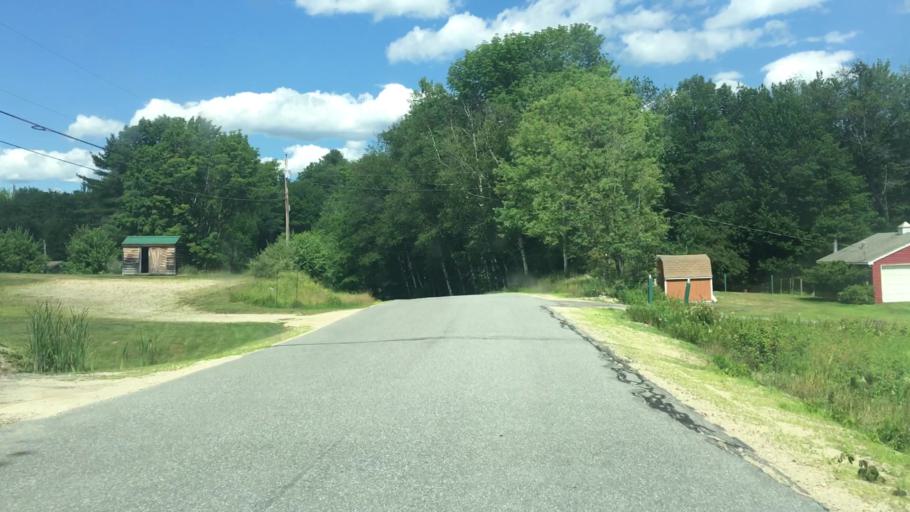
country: US
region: Maine
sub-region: Franklin County
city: Jay
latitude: 44.5367
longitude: -70.2227
